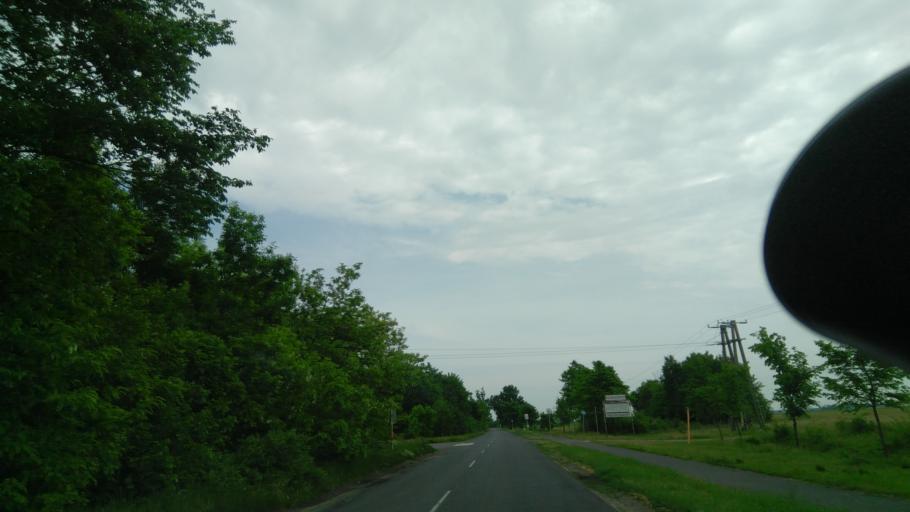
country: HU
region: Bekes
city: Szeghalom
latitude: 47.0517
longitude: 21.1926
